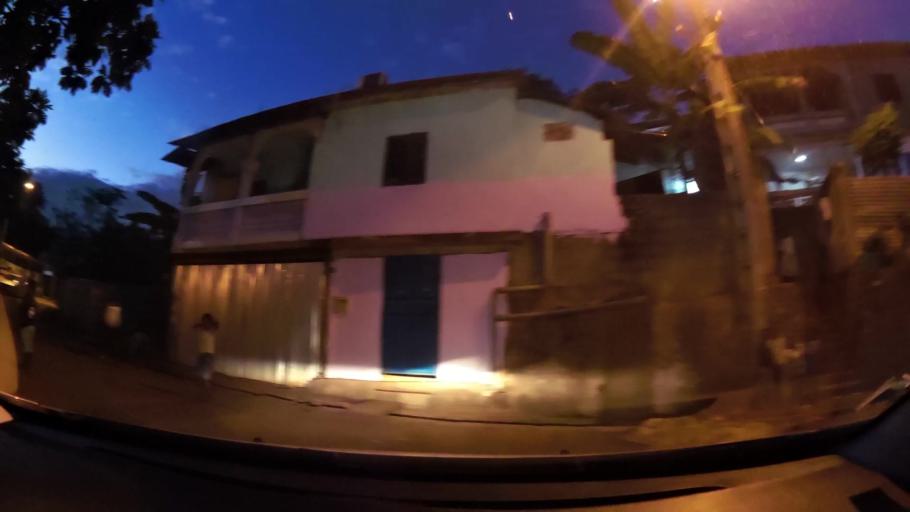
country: YT
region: Bandraboua
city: Bandraboua
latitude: -12.7184
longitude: 45.1181
